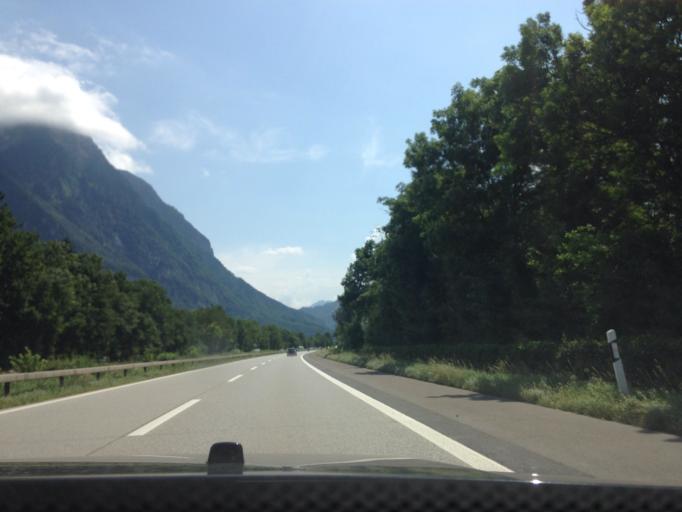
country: LI
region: Triesen
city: Triesen
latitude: 47.1001
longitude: 9.5179
